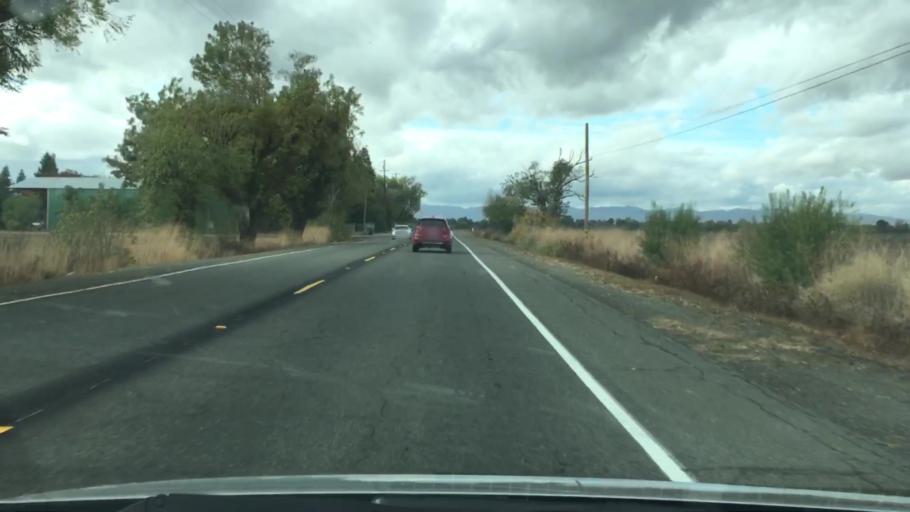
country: US
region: California
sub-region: Yolo County
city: Davis
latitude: 38.5616
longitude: -121.8296
